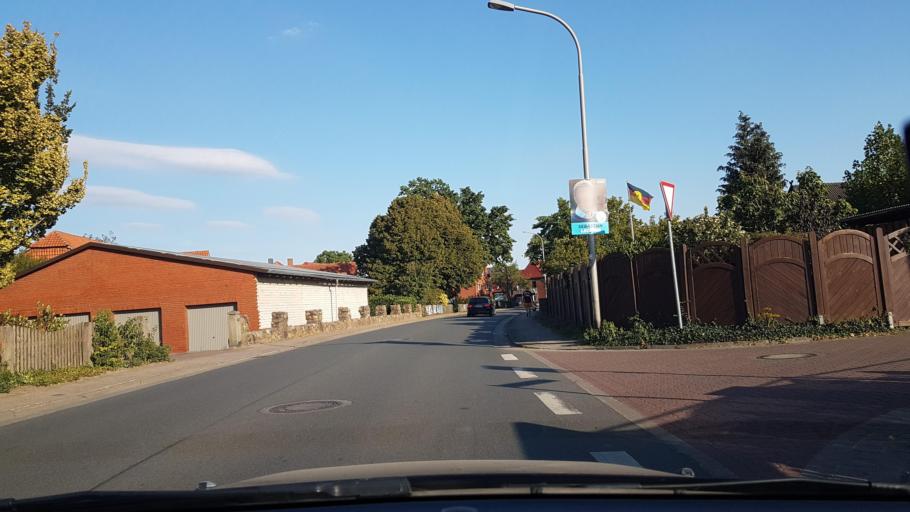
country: DE
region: Lower Saxony
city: Wunstorf
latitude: 52.4579
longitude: 9.3942
